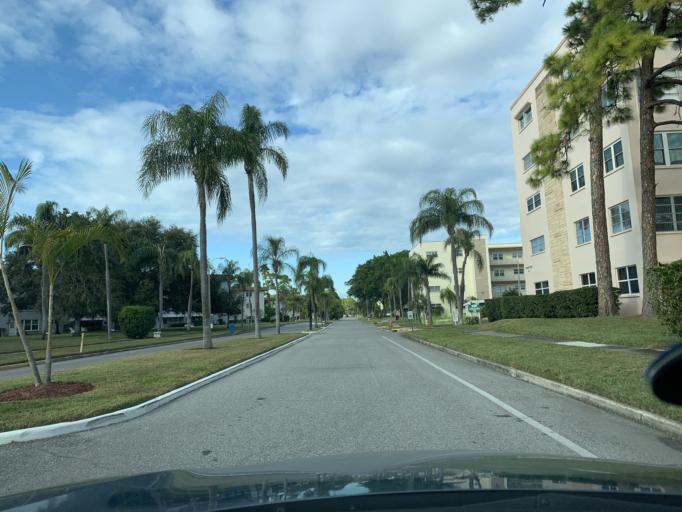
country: US
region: Florida
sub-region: Pinellas County
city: Bay Pines
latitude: 27.8228
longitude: -82.7497
